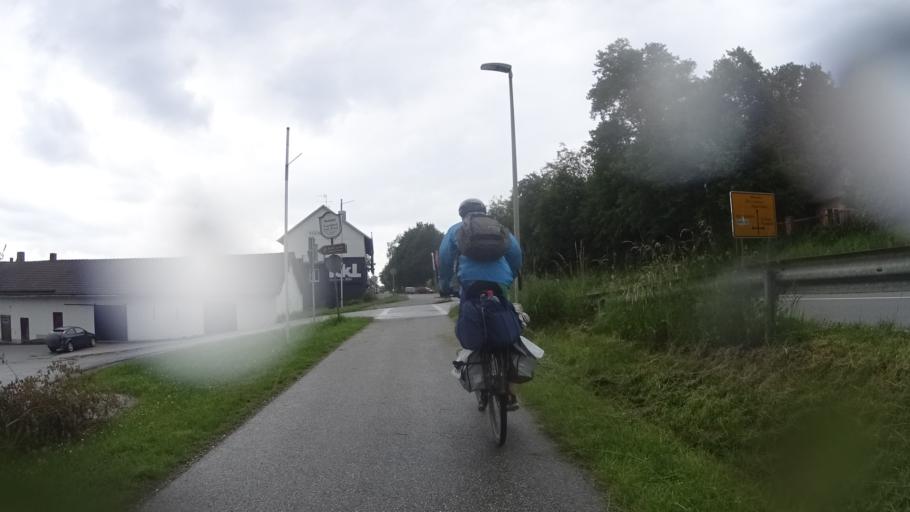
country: DE
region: Bavaria
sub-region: Lower Bavaria
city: Hebertsfelden
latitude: 48.4175
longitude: 12.8179
